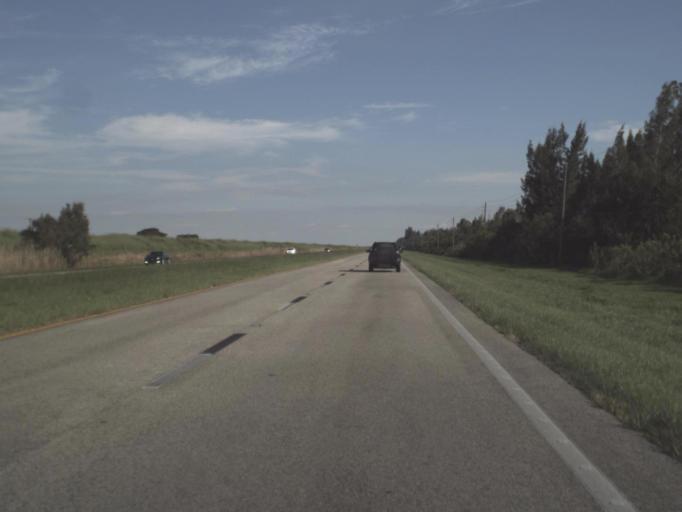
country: US
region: Florida
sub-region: Hendry County
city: Clewiston
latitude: 26.7485
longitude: -80.8974
